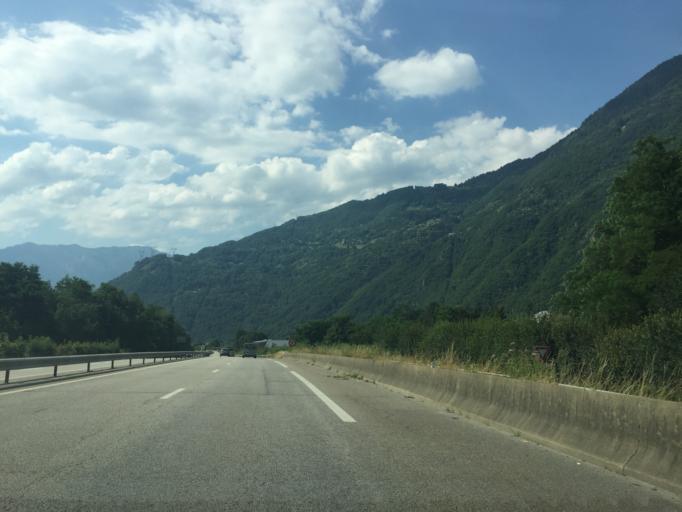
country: FR
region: Rhone-Alpes
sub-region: Departement de la Savoie
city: La Bathie
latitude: 45.6519
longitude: 6.4359
